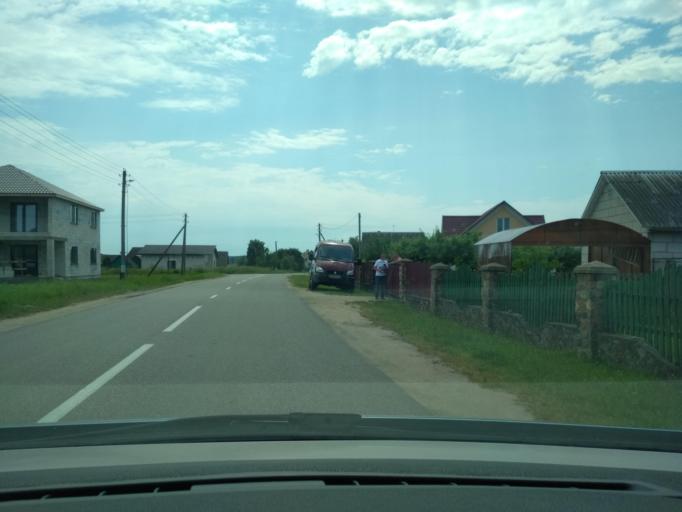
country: BY
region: Grodnenskaya
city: Astravyets
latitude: 54.6035
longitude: 25.9607
